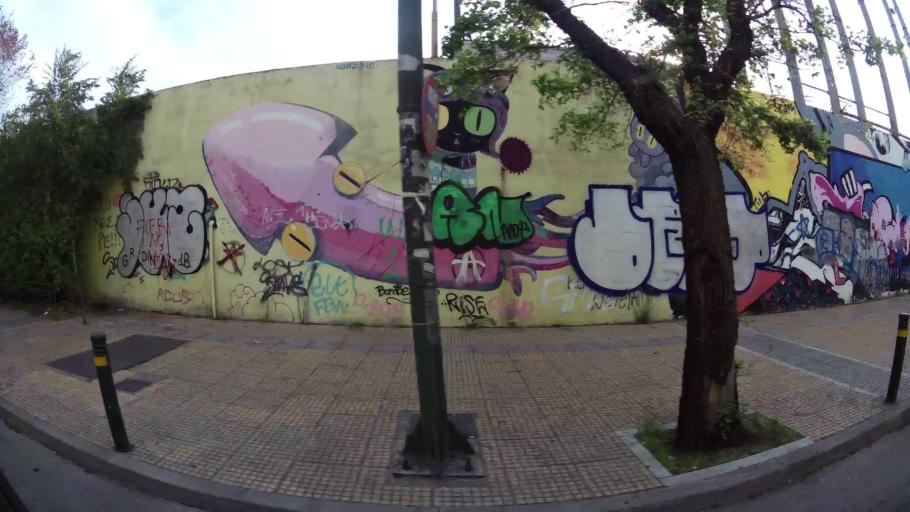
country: GR
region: Attica
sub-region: Nomarchia Athinas
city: Kipseli
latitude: 37.9978
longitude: 23.7223
